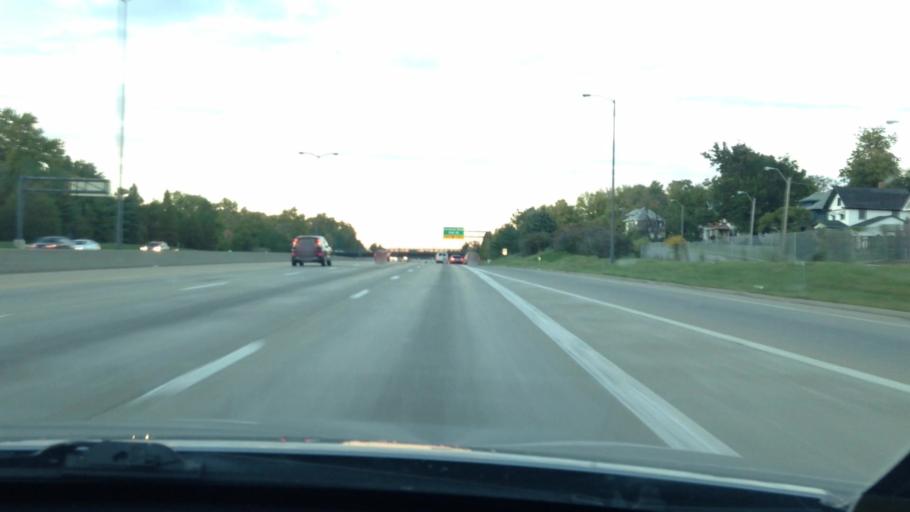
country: US
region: Missouri
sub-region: Jackson County
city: Kansas City
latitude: 39.0588
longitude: -94.5608
